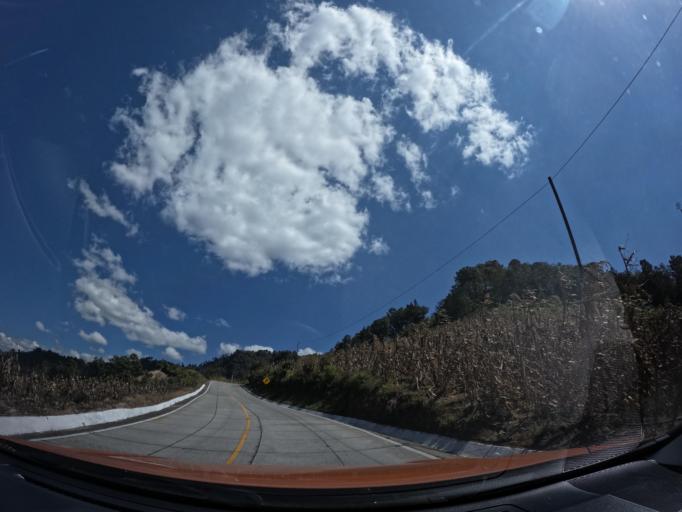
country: GT
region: Solola
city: San Antonio Palopo
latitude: 14.6914
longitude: -91.0760
